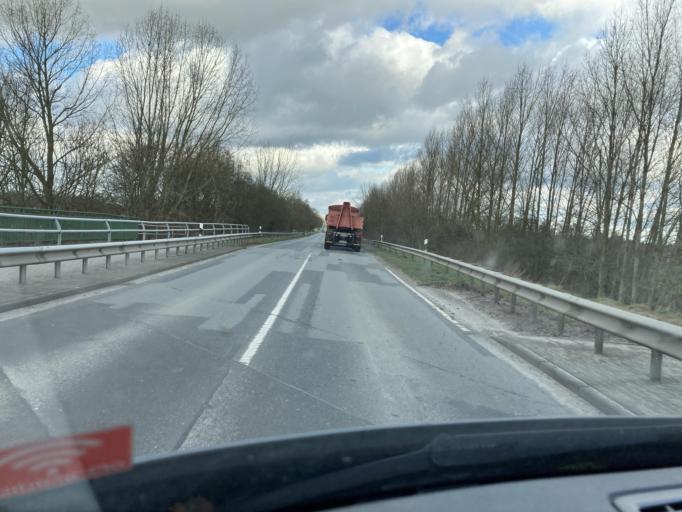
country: DE
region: Lower Saxony
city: Sande
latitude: 53.5010
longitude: 8.0242
